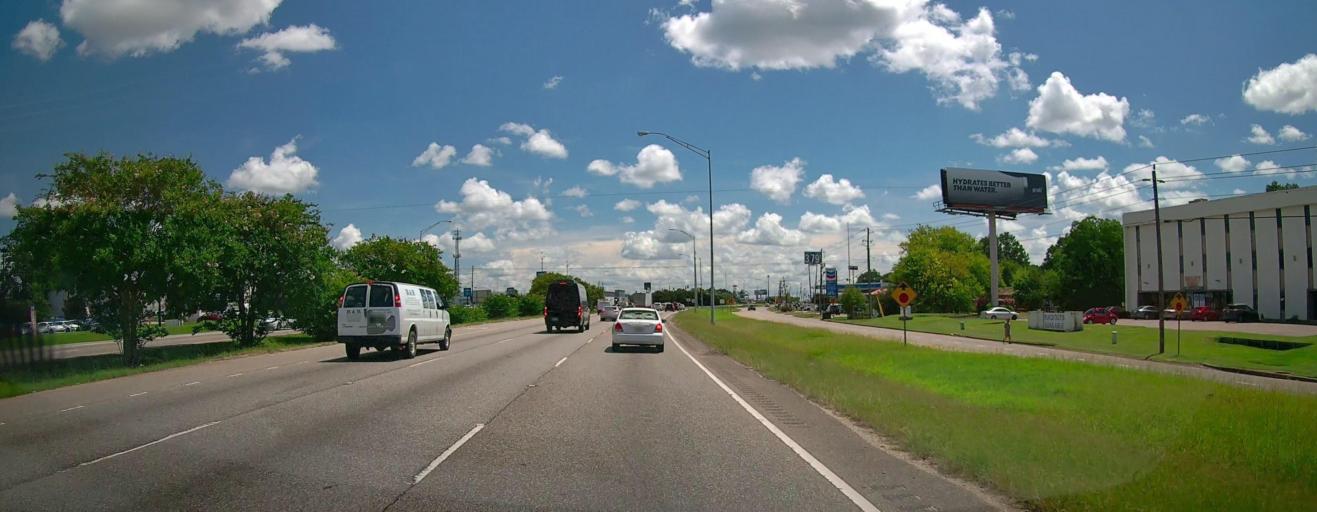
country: US
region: Alabama
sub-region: Montgomery County
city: Montgomery
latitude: 32.3730
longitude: -86.2094
